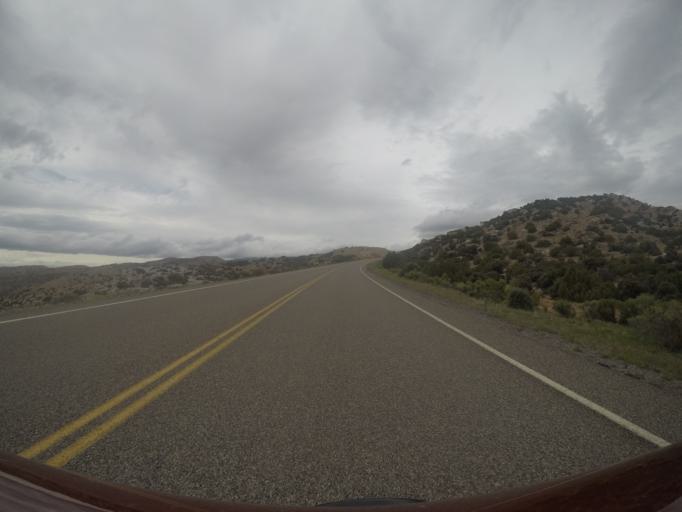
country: US
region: Wyoming
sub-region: Big Horn County
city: Lovell
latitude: 45.0019
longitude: -108.2668
